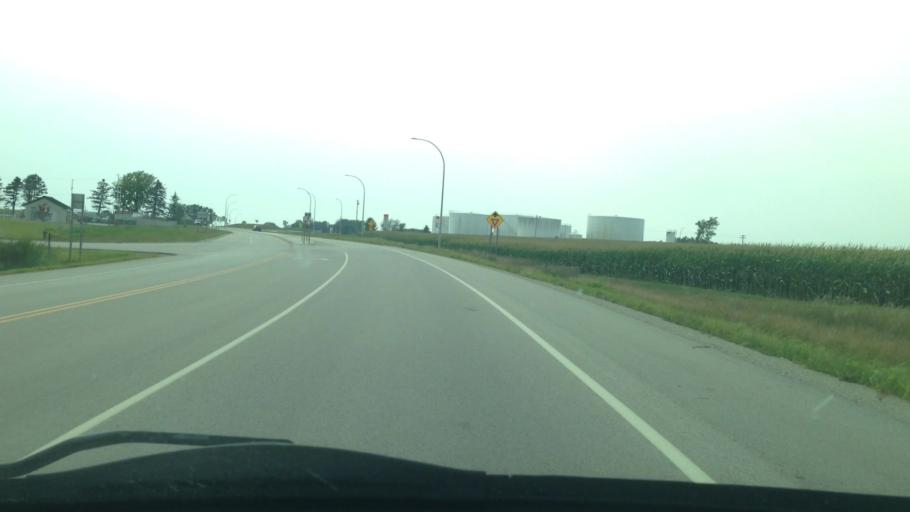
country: US
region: Minnesota
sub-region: Olmsted County
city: Eyota
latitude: 43.9990
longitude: -92.2451
